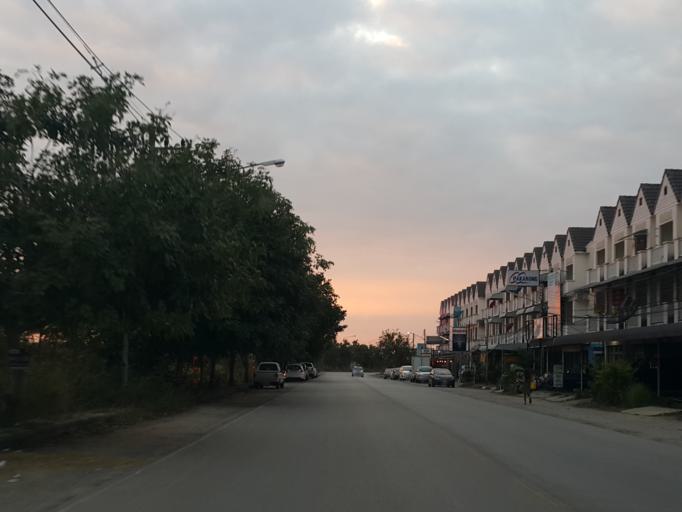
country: TH
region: Lampang
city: Lampang
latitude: 18.2638
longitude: 99.4931
